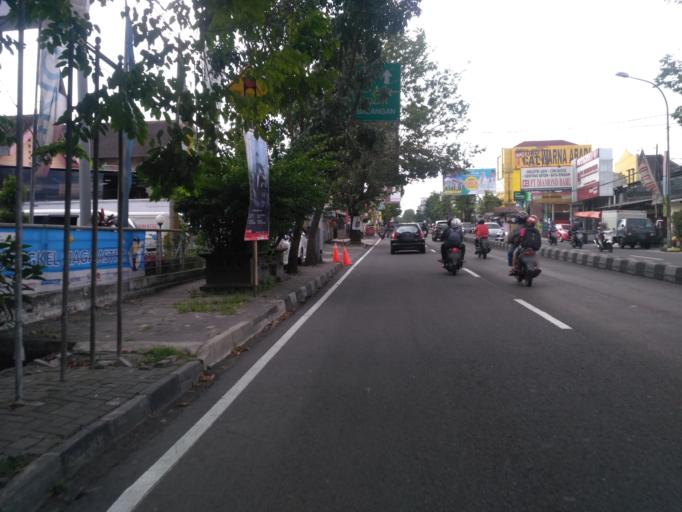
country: ID
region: Daerah Istimewa Yogyakarta
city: Melati
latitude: -7.7419
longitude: 110.3627
